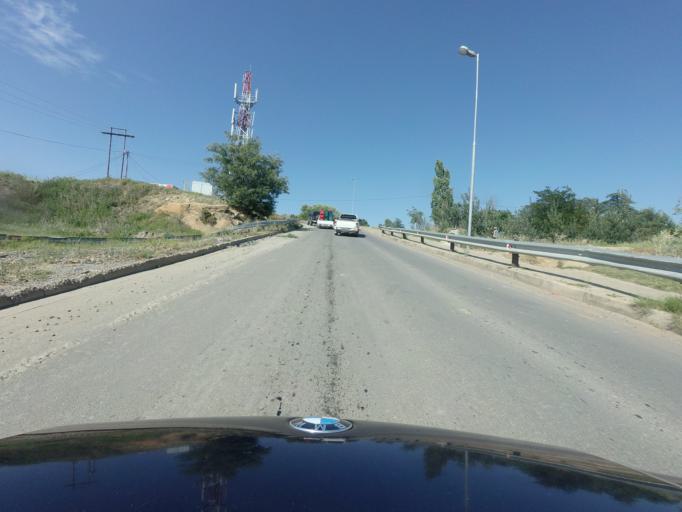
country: LS
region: Maseru
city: Maseru
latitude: -29.3047
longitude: 27.4873
